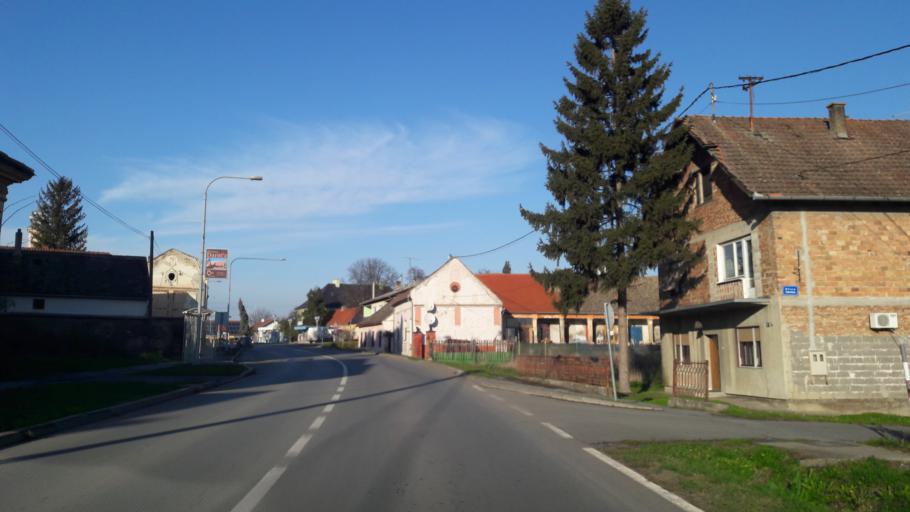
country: HR
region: Osjecko-Baranjska
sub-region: Grad Osijek
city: Bilje
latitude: 45.6021
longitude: 18.7440
